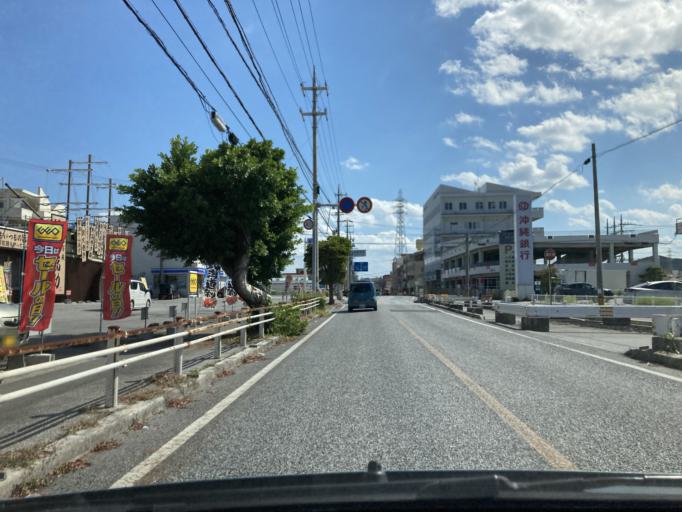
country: JP
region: Okinawa
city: Tomigusuku
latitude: 26.1911
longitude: 127.7080
